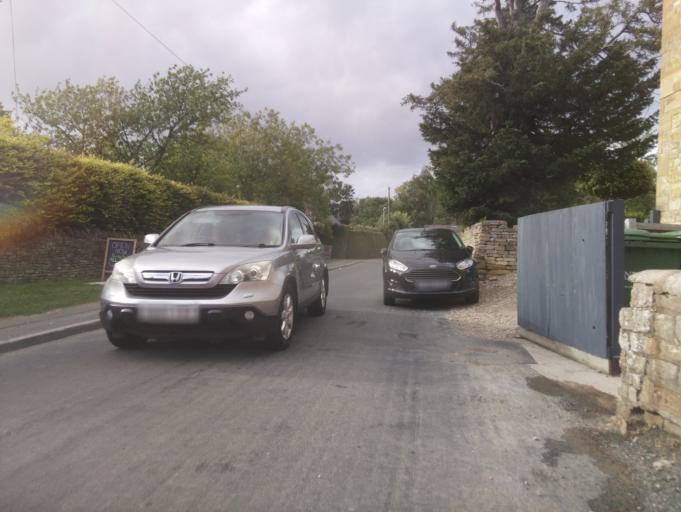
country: GB
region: England
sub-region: Gloucestershire
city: Chipping Campden
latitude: 52.0386
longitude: -1.7322
